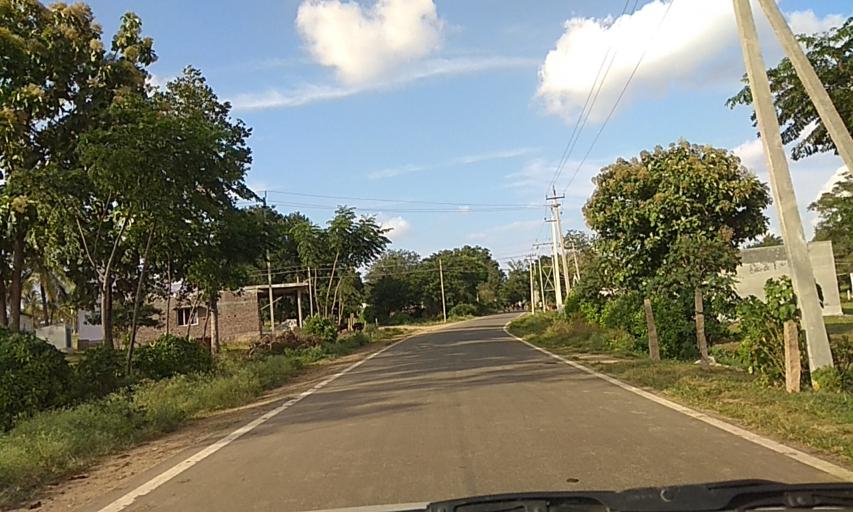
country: IN
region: Karnataka
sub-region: Chamrajnagar
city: Gundlupet
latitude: 11.7603
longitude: 76.7702
